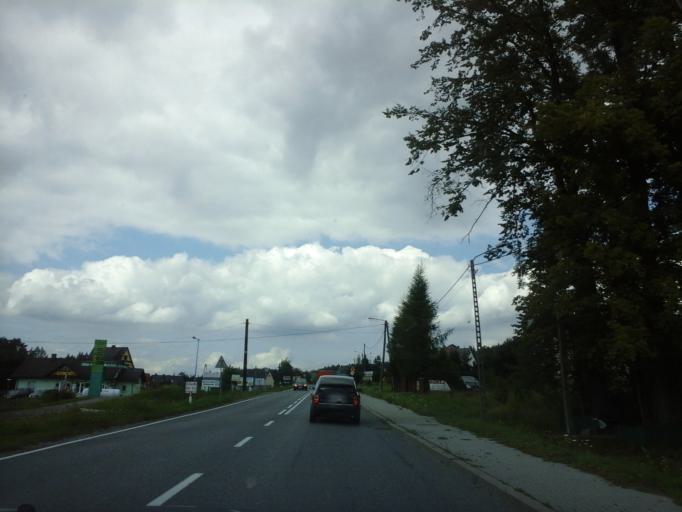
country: PL
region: Lesser Poland Voivodeship
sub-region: Powiat suski
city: Jordanow
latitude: 49.6573
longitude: 19.8104
